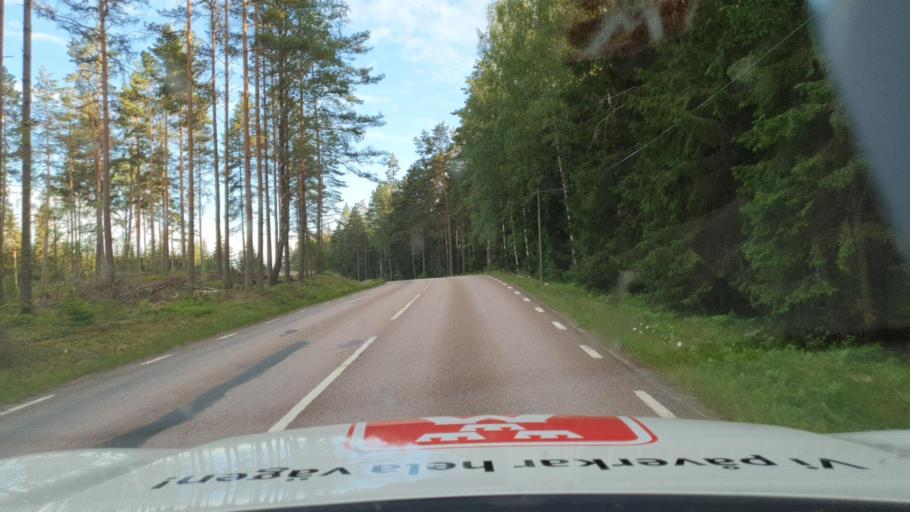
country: SE
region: Vaermland
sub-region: Karlstads Kommun
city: Skattkarr
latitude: 59.4368
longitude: 13.8353
